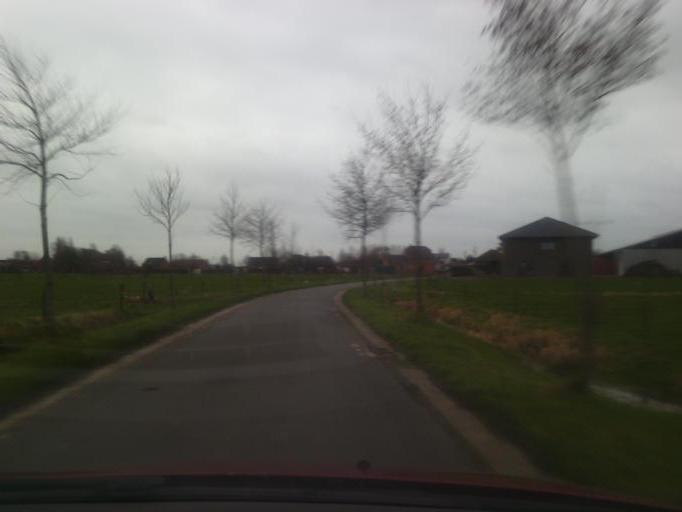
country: BE
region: Flanders
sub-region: Provincie Oost-Vlaanderen
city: Lokeren
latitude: 51.0714
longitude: 4.0059
